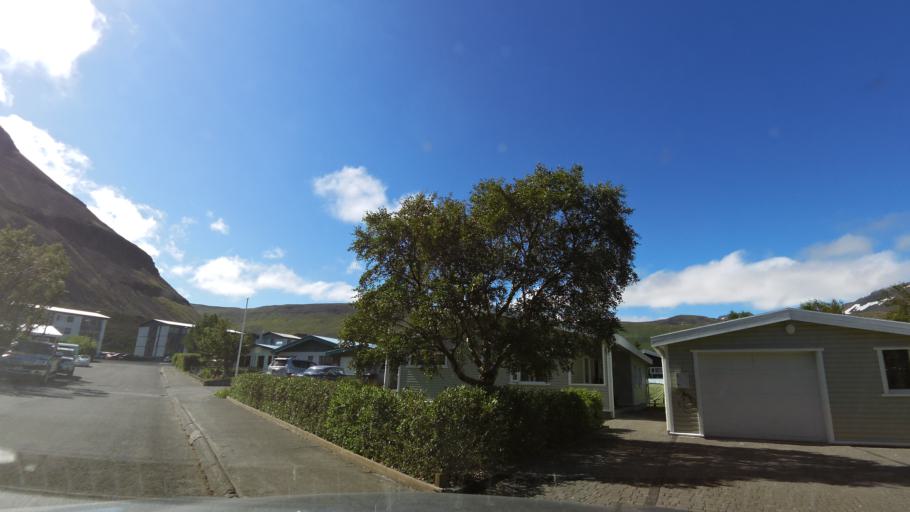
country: IS
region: Westfjords
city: Isafjoerdur
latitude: 66.0555
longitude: -23.1740
